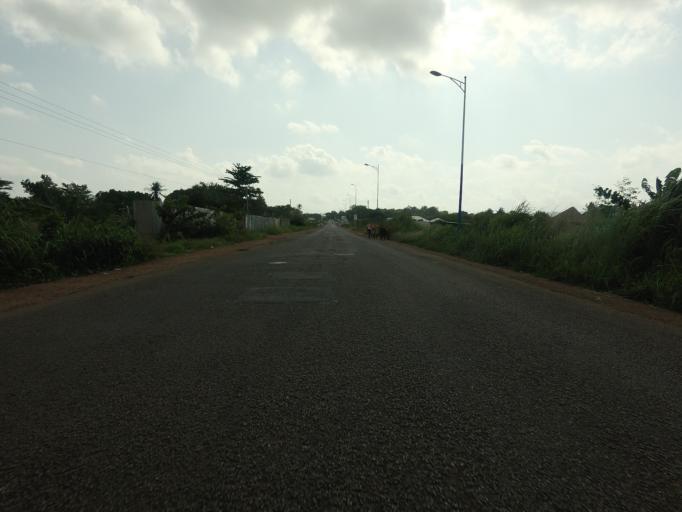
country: GH
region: Volta
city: Ho
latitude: 6.6001
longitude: 0.5049
